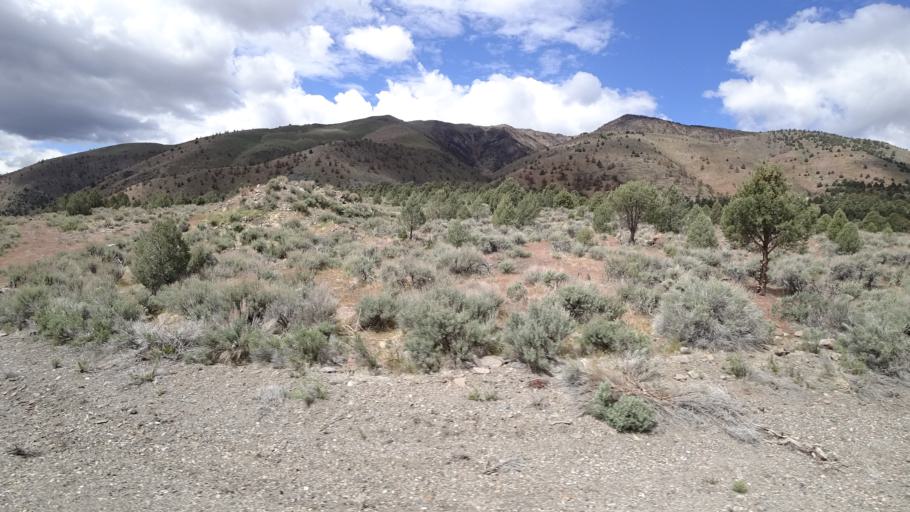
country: US
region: Nevada
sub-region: Lyon County
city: Smith Valley
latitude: 38.6967
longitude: -119.5491
